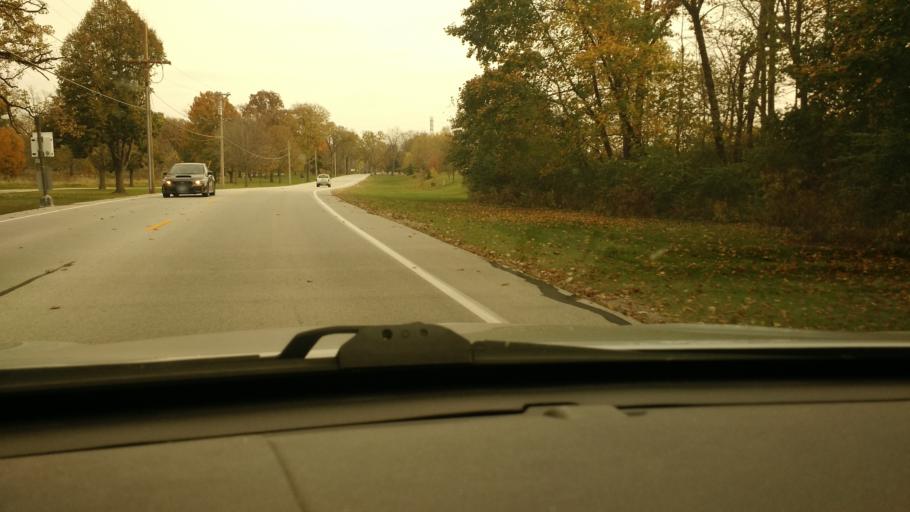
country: US
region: Iowa
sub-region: Scott County
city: Bettendorf
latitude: 41.5177
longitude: -90.5296
